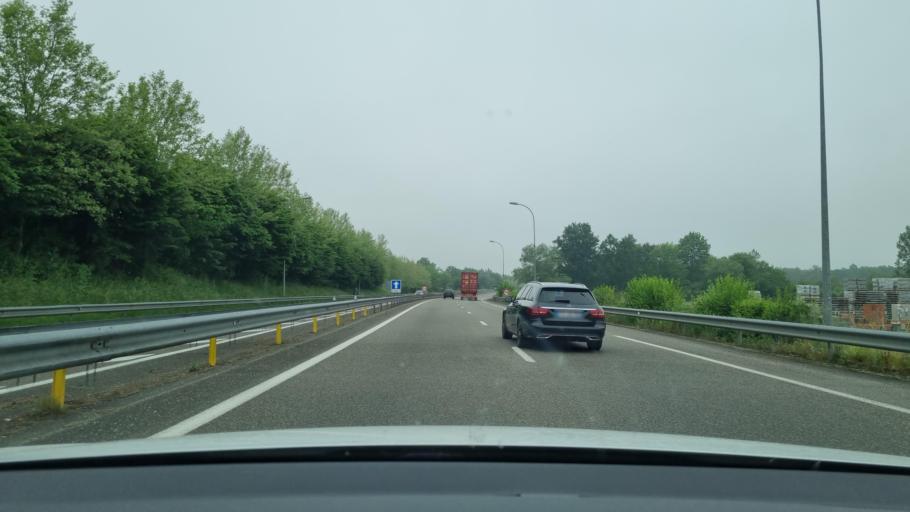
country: FR
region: Aquitaine
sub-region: Departement des Landes
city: Saint-Sever
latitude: 43.7762
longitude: -0.5568
